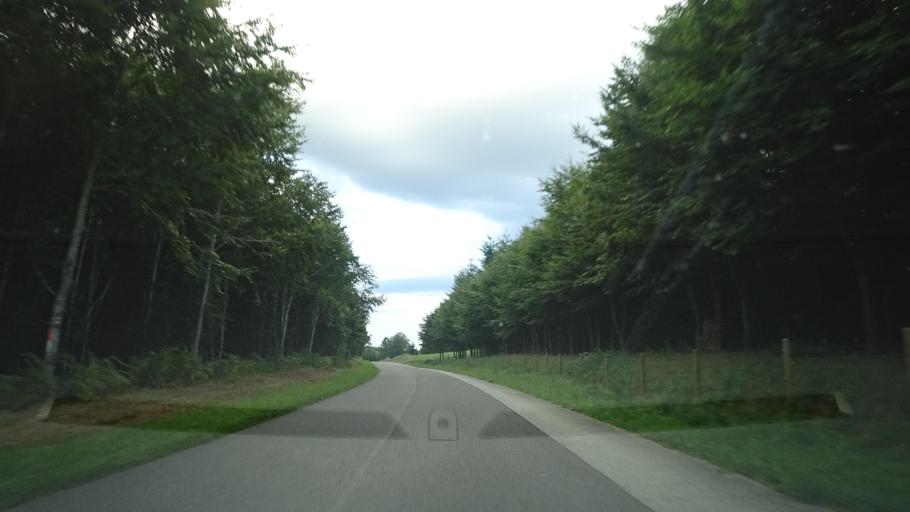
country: BE
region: Wallonia
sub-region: Province du Luxembourg
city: Bertrix
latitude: 49.8087
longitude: 5.2911
